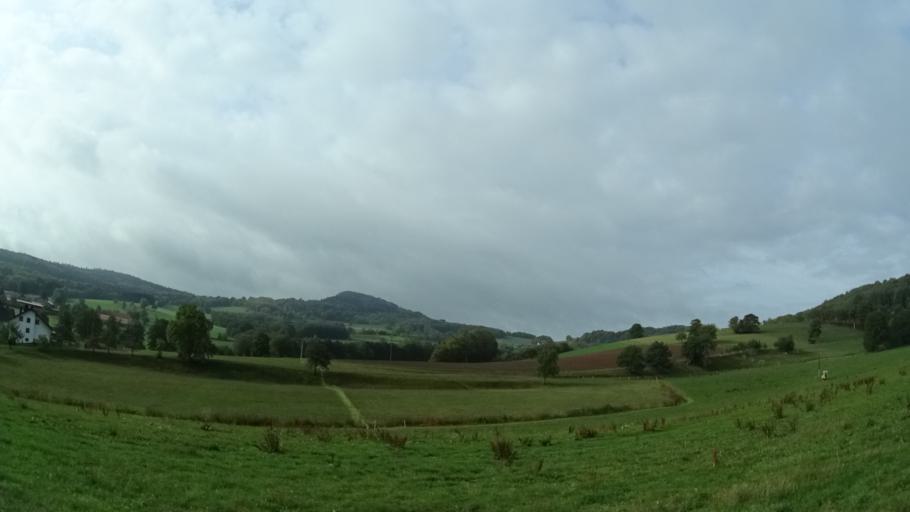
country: DE
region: Hesse
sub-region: Regierungsbezirk Kassel
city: Hilders
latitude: 50.5635
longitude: 9.9206
